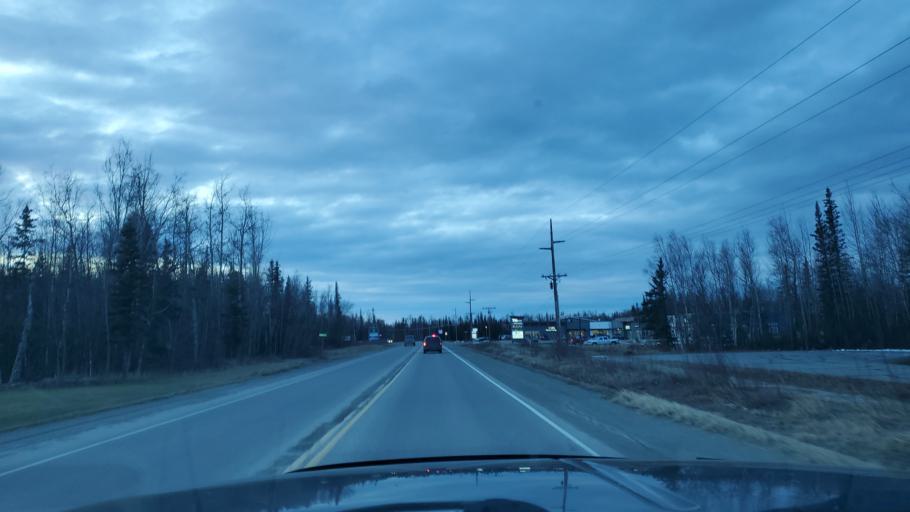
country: US
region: Alaska
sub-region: Matanuska-Susitna Borough
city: Wasilla
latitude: 61.5889
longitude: -149.4074
